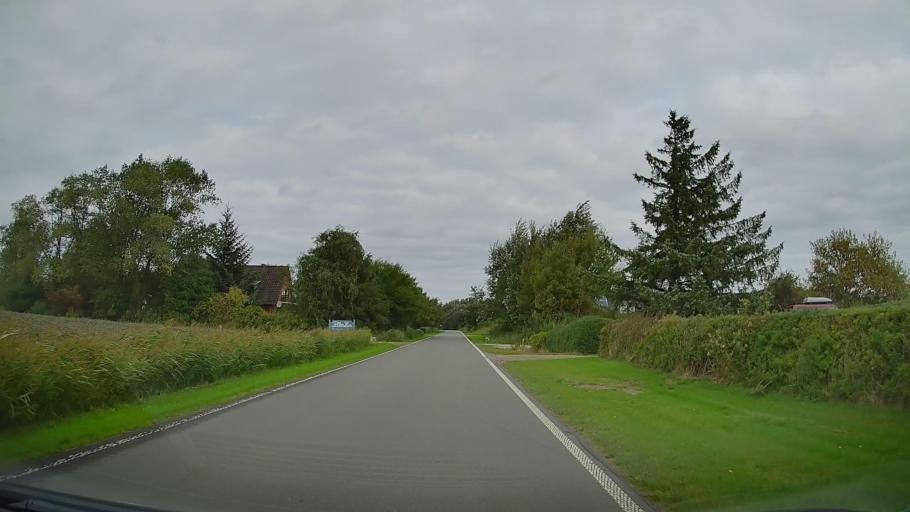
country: DE
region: Schleswig-Holstein
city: Klanxbull
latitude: 54.8835
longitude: 8.6826
